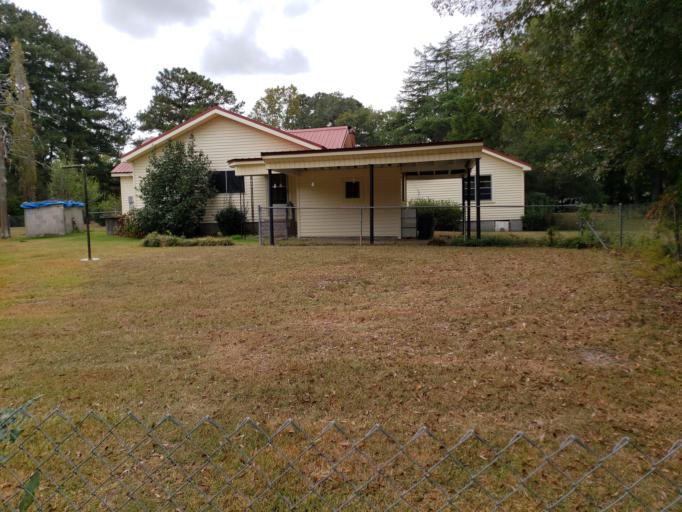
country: US
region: Georgia
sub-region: Troup County
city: La Grange
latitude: 32.9833
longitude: -84.9947
